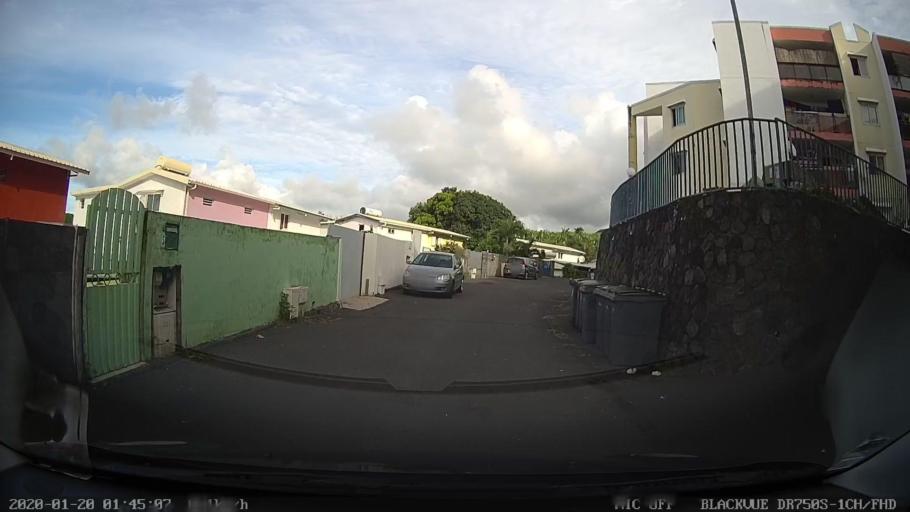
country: RE
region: Reunion
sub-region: Reunion
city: Sainte-Marie
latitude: -20.9272
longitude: 55.5272
